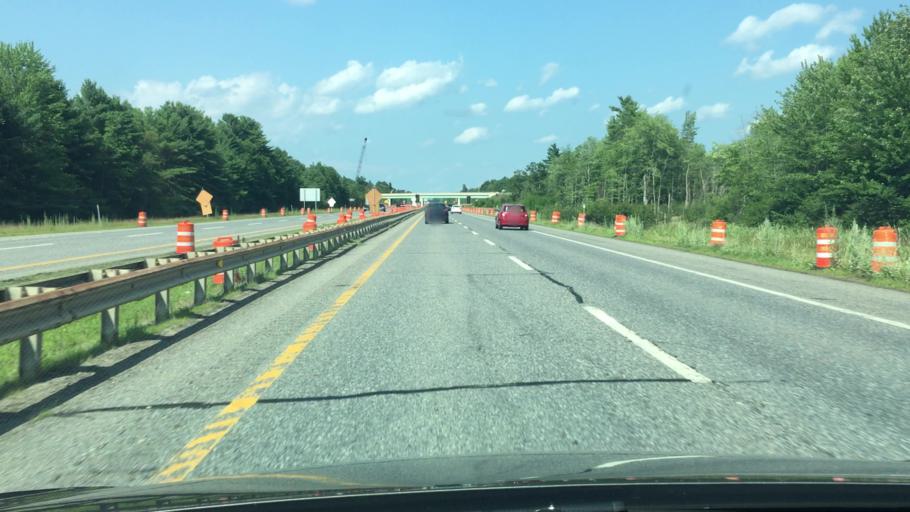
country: US
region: Maine
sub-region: Kennebec County
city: Gardiner
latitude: 44.2143
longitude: -69.8272
